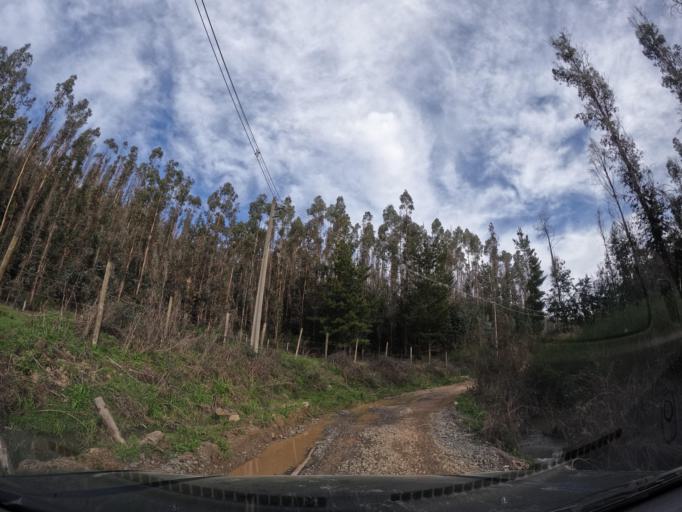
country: CL
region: Biobio
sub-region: Provincia de Concepcion
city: Chiguayante
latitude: -37.0190
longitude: -72.9139
